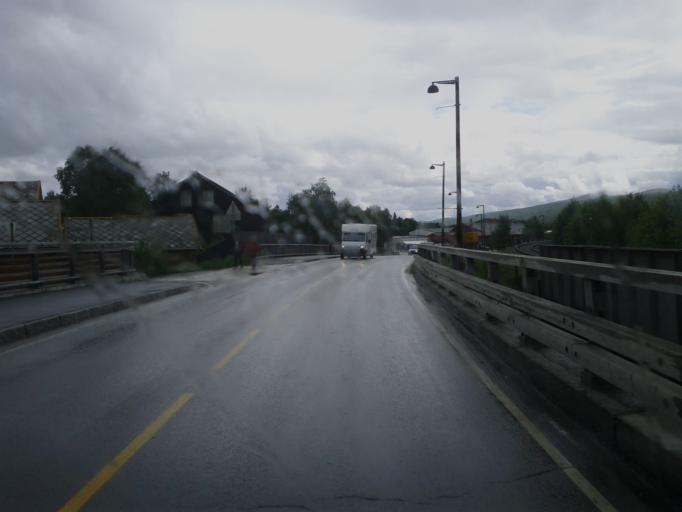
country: NO
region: Sor-Trondelag
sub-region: Roros
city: Roros
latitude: 62.5734
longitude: 11.3857
